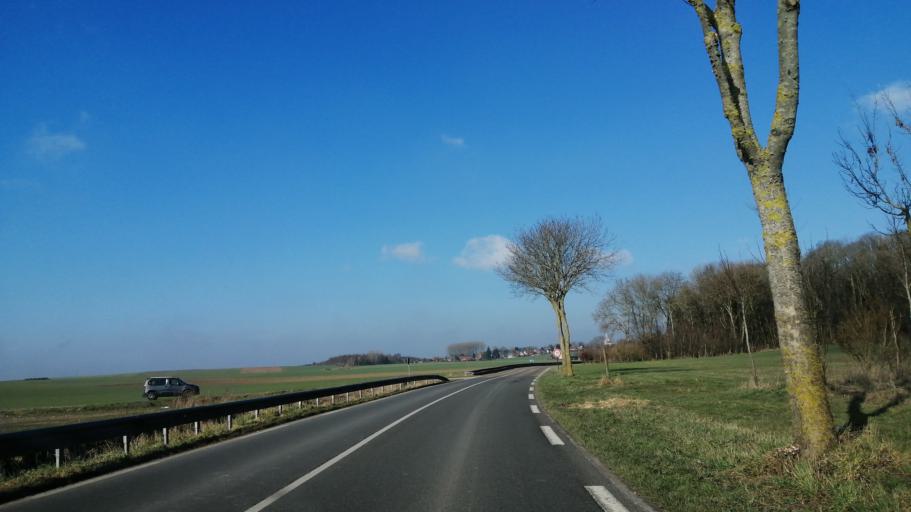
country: FR
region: Nord-Pas-de-Calais
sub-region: Departement du Pas-de-Calais
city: Mont-Saint-Eloi
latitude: 50.3651
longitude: 2.6511
